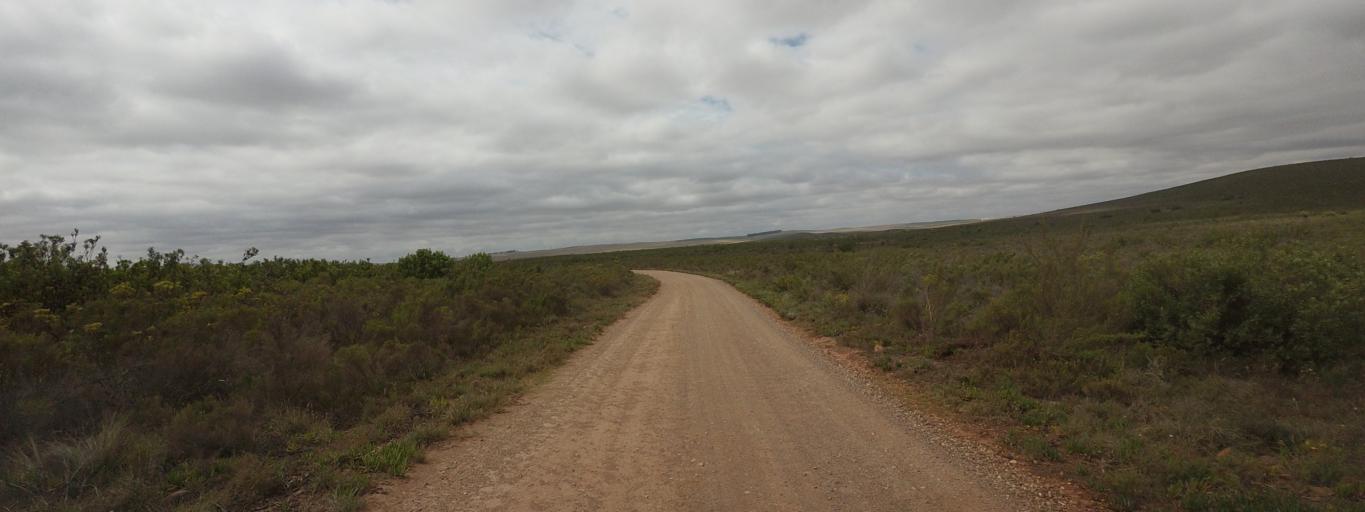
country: ZA
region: Western Cape
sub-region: Overberg District Municipality
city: Swellendam
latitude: -34.0606
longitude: 20.4331
